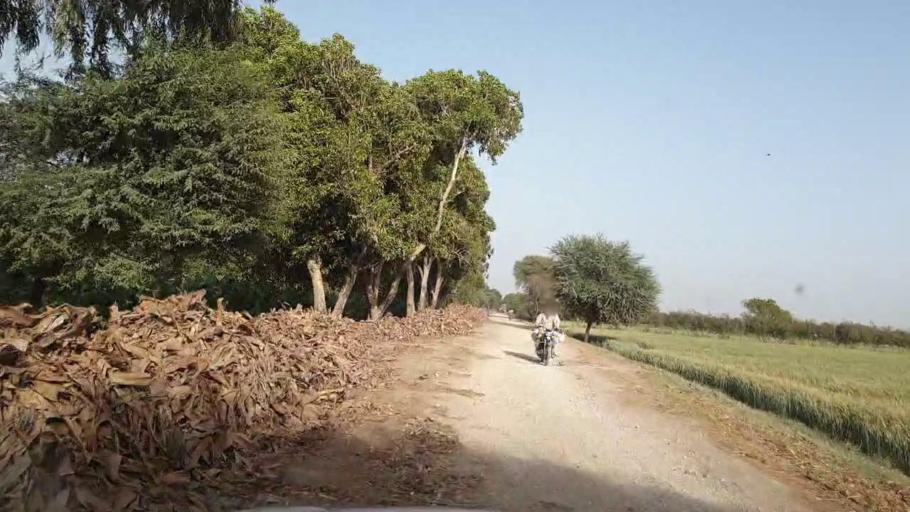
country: PK
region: Sindh
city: Tando Ghulam Ali
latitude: 25.0819
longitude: 68.8868
